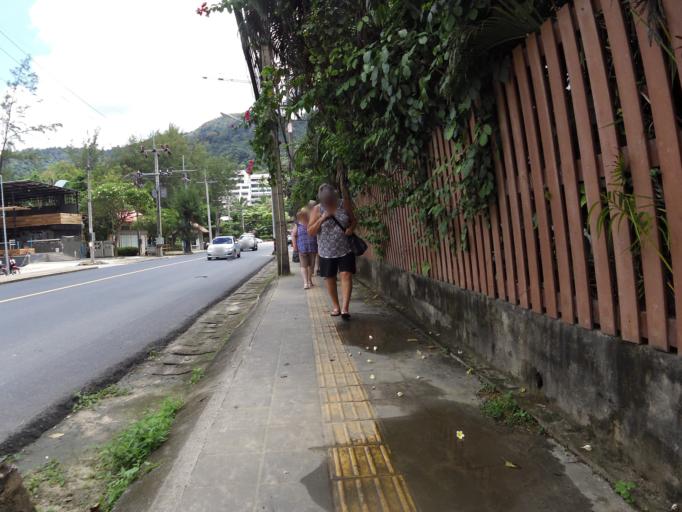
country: TH
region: Phuket
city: Ban Karon
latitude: 7.8507
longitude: 98.2937
